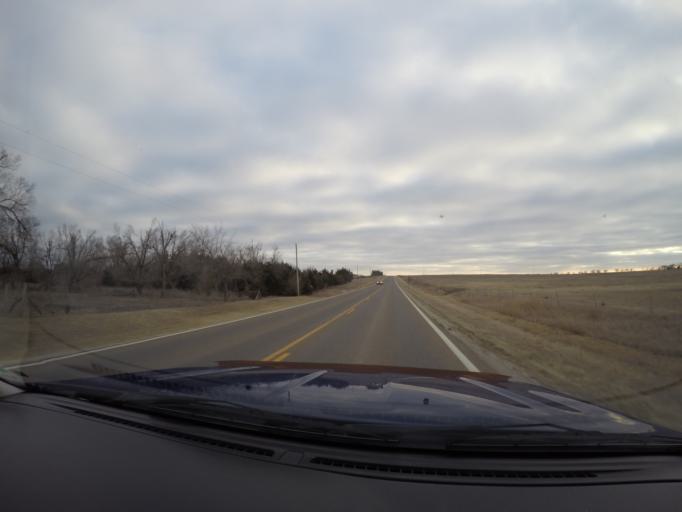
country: US
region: Kansas
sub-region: Morris County
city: Council Grove
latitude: 38.8008
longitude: -96.5013
